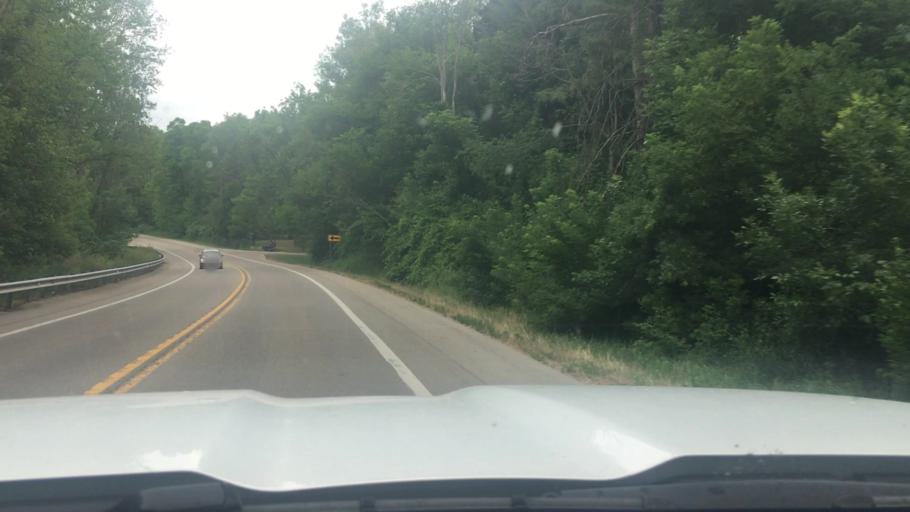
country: US
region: Michigan
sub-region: Ionia County
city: Ionia
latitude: 42.9775
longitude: -85.1183
